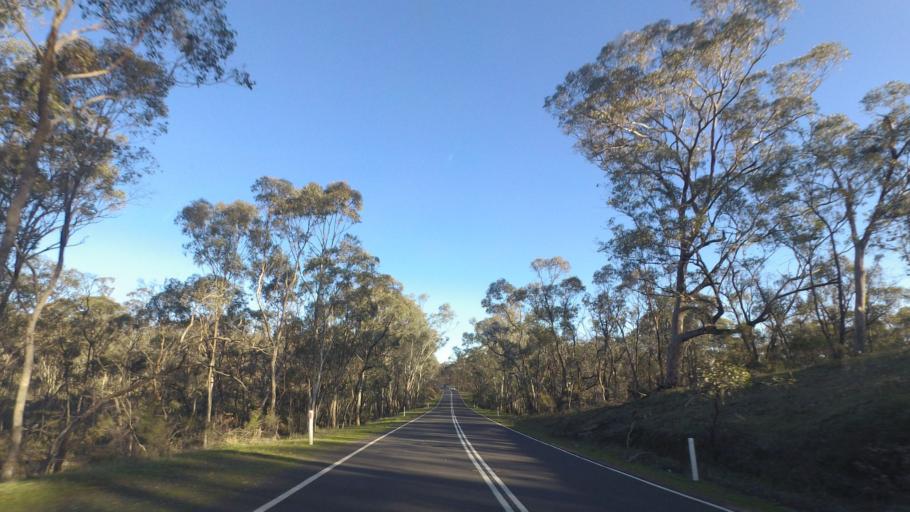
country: AU
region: Victoria
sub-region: Greater Bendigo
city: Kennington
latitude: -36.9158
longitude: 144.4923
